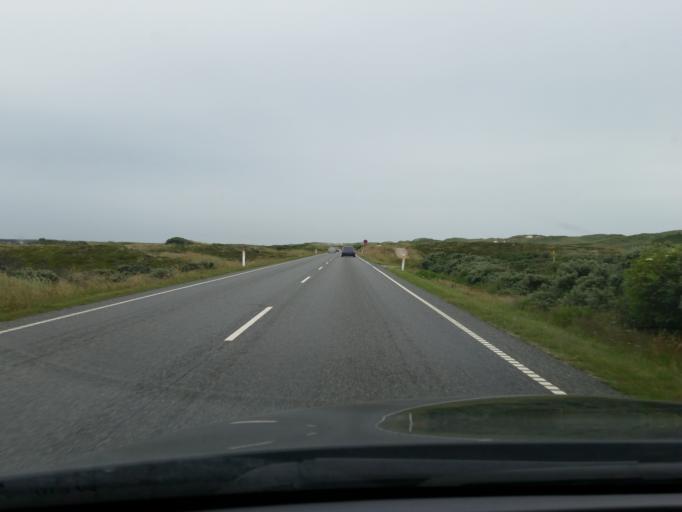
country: DK
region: Central Jutland
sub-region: Ringkobing-Skjern Kommune
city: Hvide Sande
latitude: 55.8322
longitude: 8.1727
